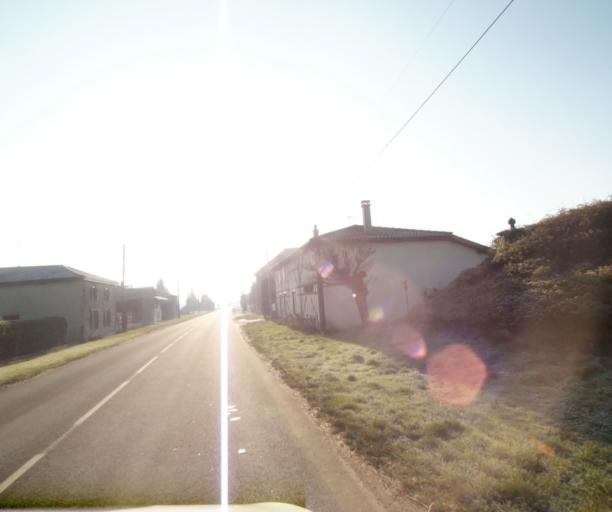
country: FR
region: Champagne-Ardenne
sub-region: Departement de la Haute-Marne
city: Montier-en-Der
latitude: 48.4600
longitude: 4.7680
